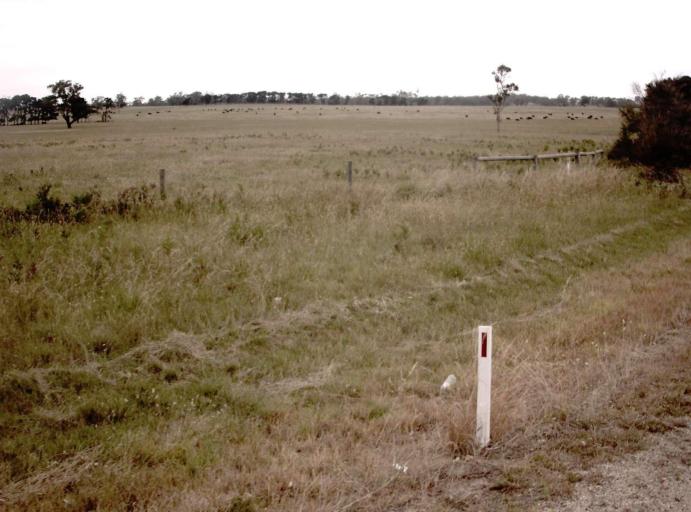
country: AU
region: Victoria
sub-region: Wellington
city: Sale
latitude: -38.1688
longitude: 147.1048
